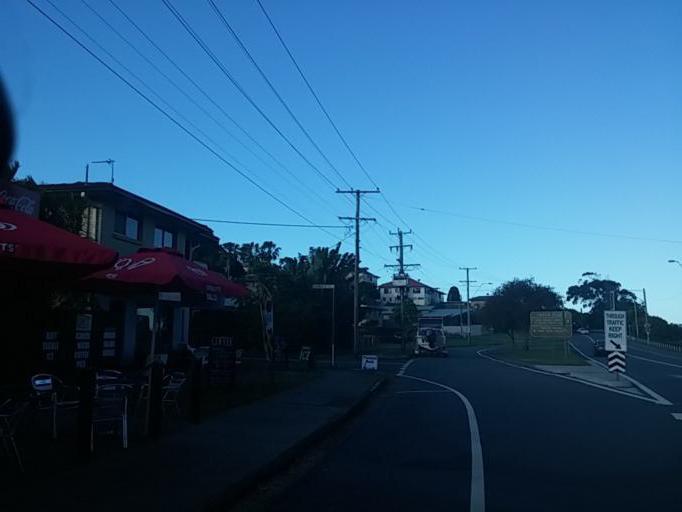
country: AU
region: New South Wales
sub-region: Tweed
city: Tweed Heads West
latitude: -28.1854
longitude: 153.5333
